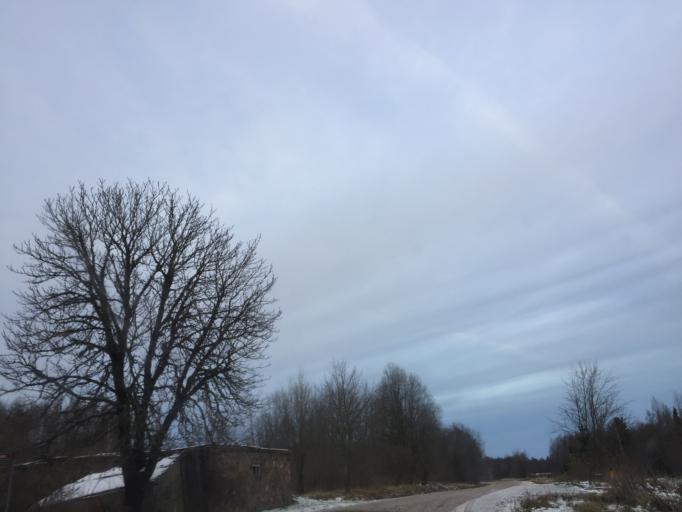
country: LV
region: Limbazu Rajons
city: Limbazi
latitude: 57.5703
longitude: 24.8215
